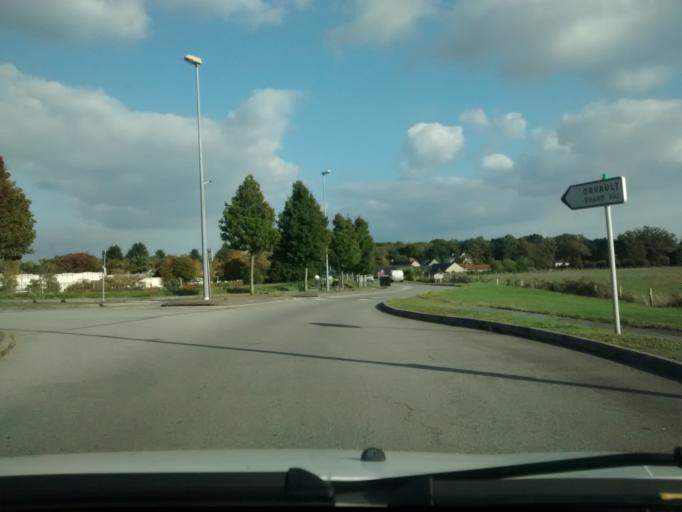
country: FR
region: Pays de la Loire
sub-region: Departement de la Loire-Atlantique
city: Orvault
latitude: 47.2695
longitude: -1.6142
